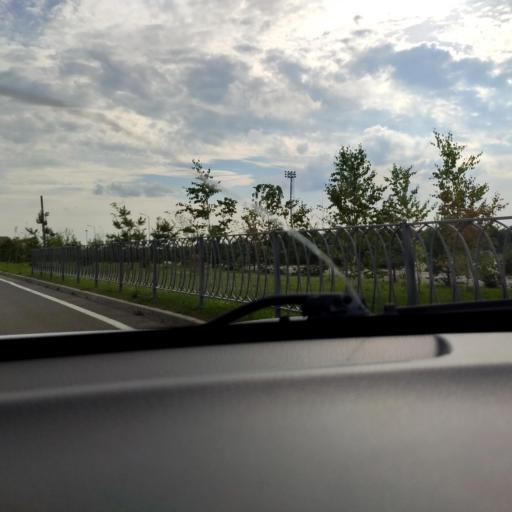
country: RU
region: Tatarstan
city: Sviyazhsk
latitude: 55.7503
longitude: 48.7429
